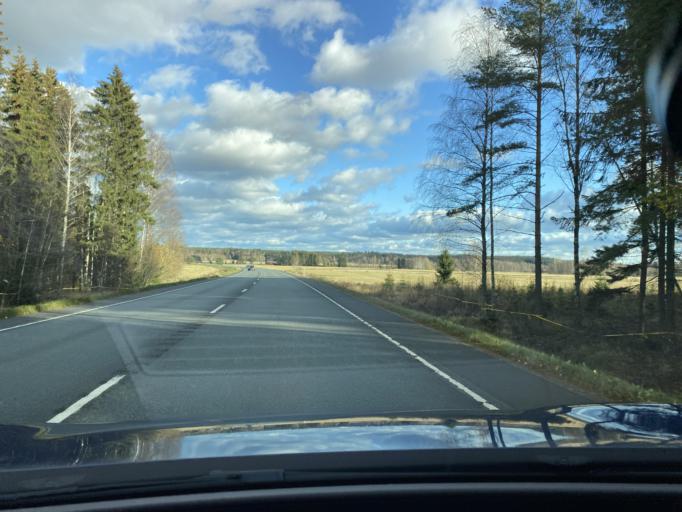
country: FI
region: Haeme
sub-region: Riihimaeki
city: Hausjaervi
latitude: 60.7844
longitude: 24.9138
